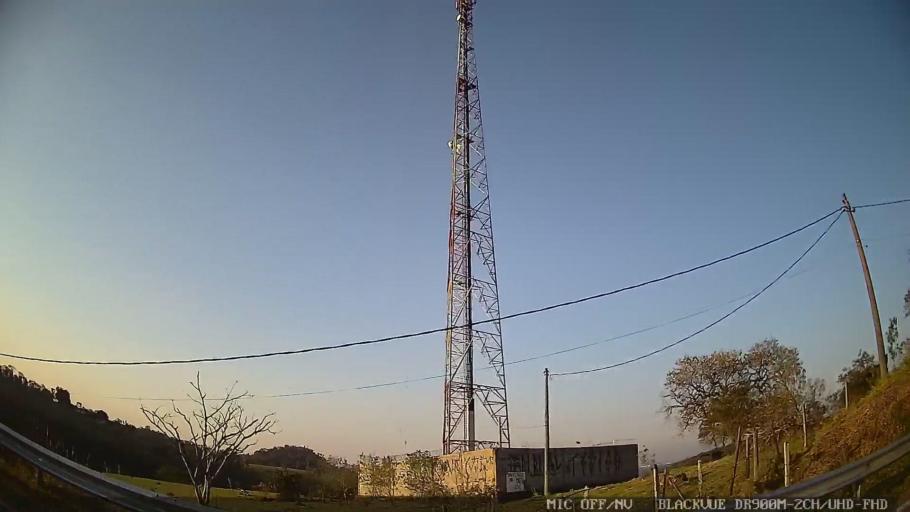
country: BR
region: Sao Paulo
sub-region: Itupeva
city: Itupeva
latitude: -23.2382
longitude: -47.0476
